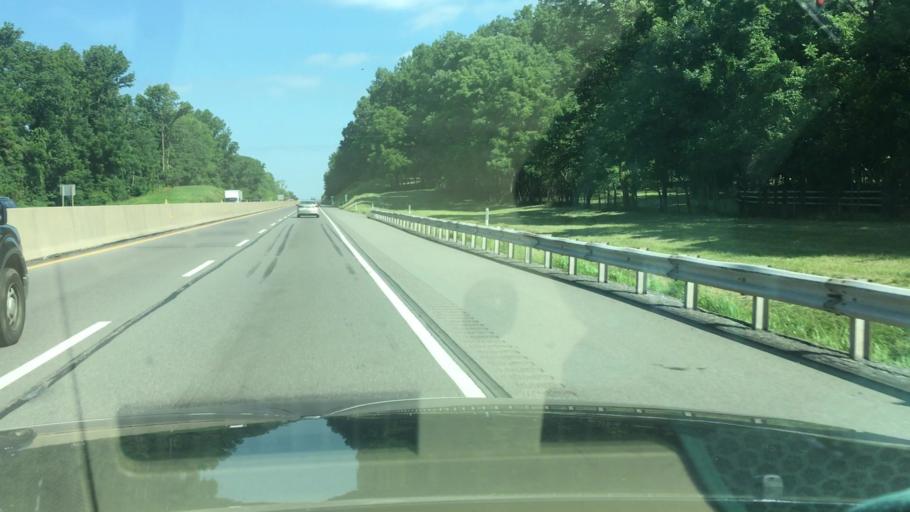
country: US
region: Pennsylvania
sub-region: Bucks County
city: Spinnerstown
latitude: 40.4552
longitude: -75.4401
